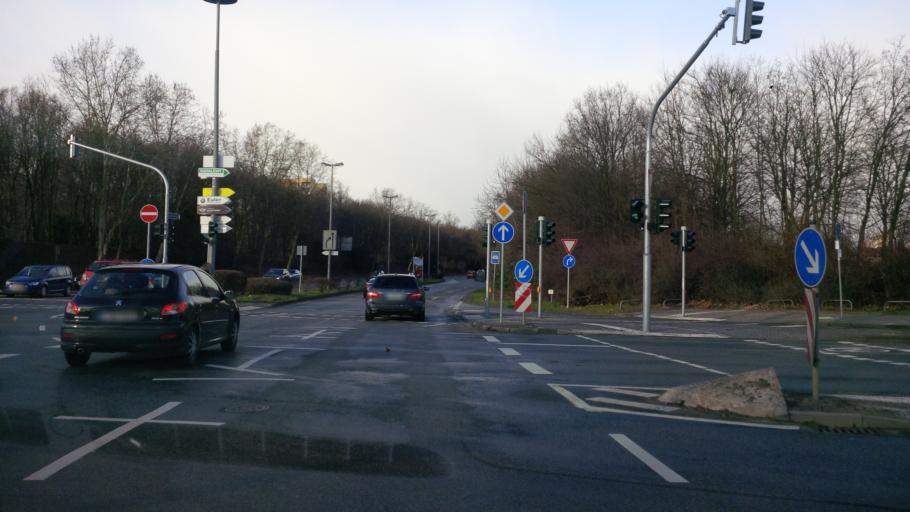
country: DE
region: Hesse
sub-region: Regierungsbezirk Darmstadt
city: Frankfurt am Main
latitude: 50.1496
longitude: 8.6760
